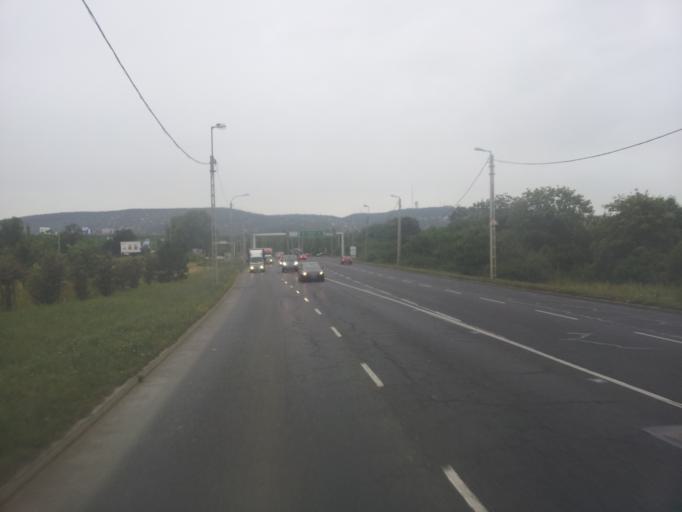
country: HU
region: Pest
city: Budaors
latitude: 47.4542
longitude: 18.9956
